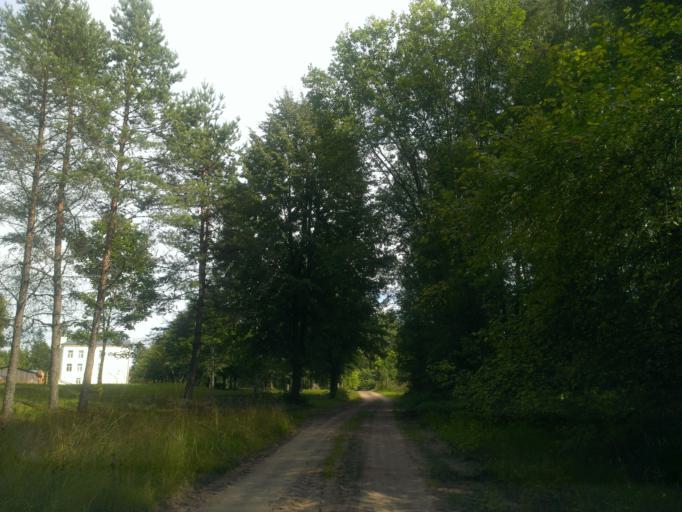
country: LV
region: Ligatne
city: Ligatne
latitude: 57.2347
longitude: 25.0311
